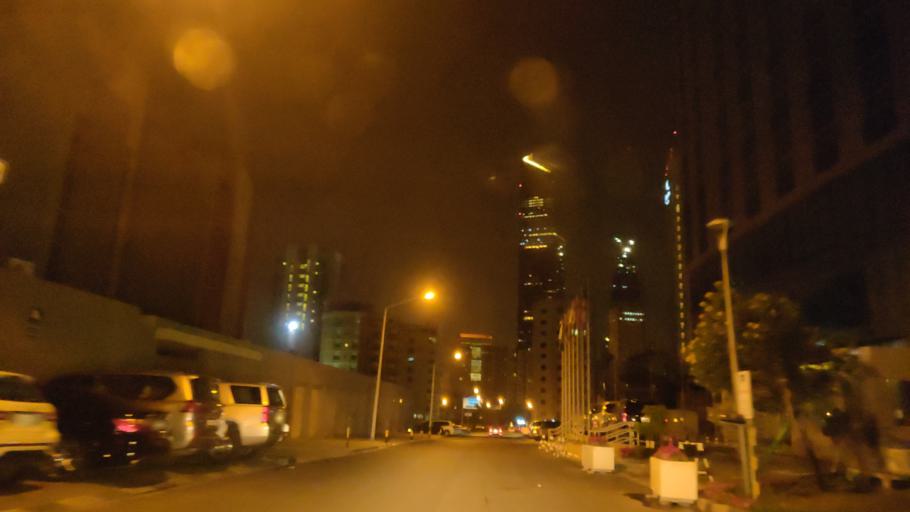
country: KW
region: Al Asimah
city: Kuwait City
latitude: 29.3886
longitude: 47.9910
